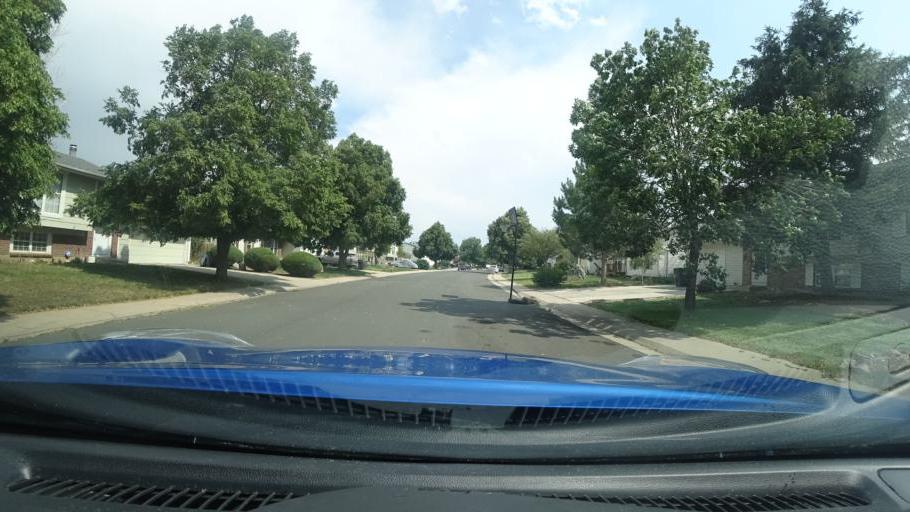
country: US
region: Colorado
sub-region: Adams County
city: Aurora
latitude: 39.6952
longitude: -104.7650
